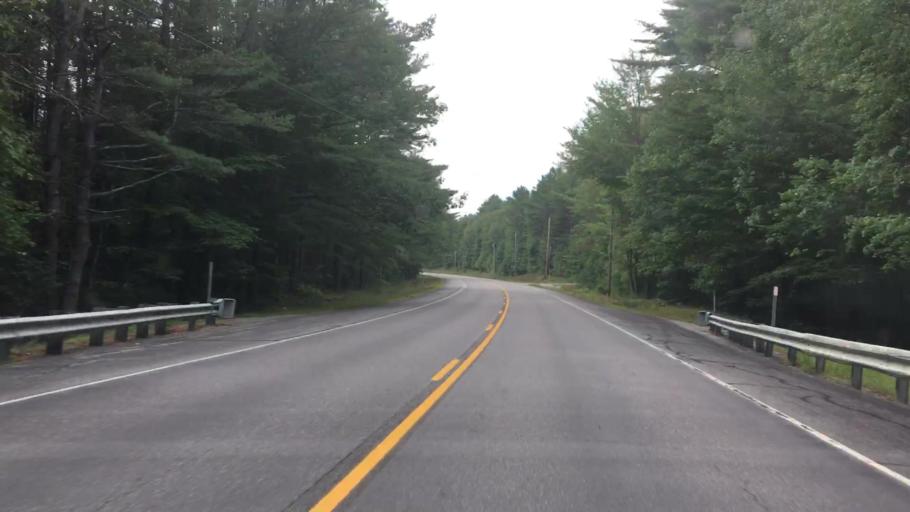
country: US
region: Maine
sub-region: Oxford County
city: Bethel
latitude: 44.4868
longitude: -70.7488
